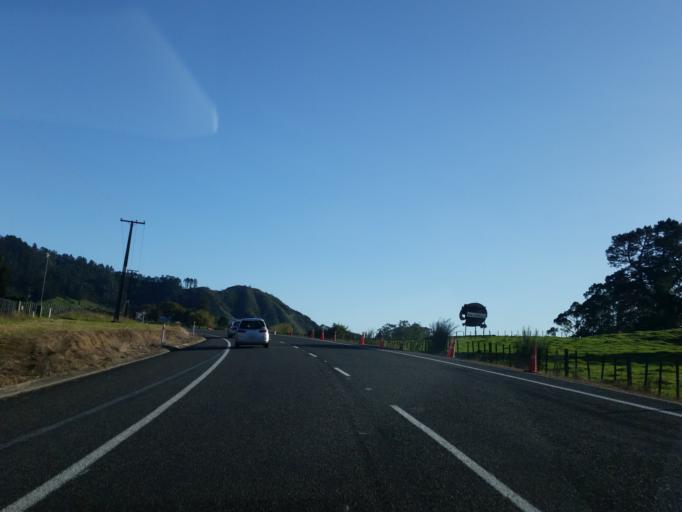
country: NZ
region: Bay of Plenty
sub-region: Western Bay of Plenty District
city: Waihi Beach
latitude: -37.4632
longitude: 175.9367
